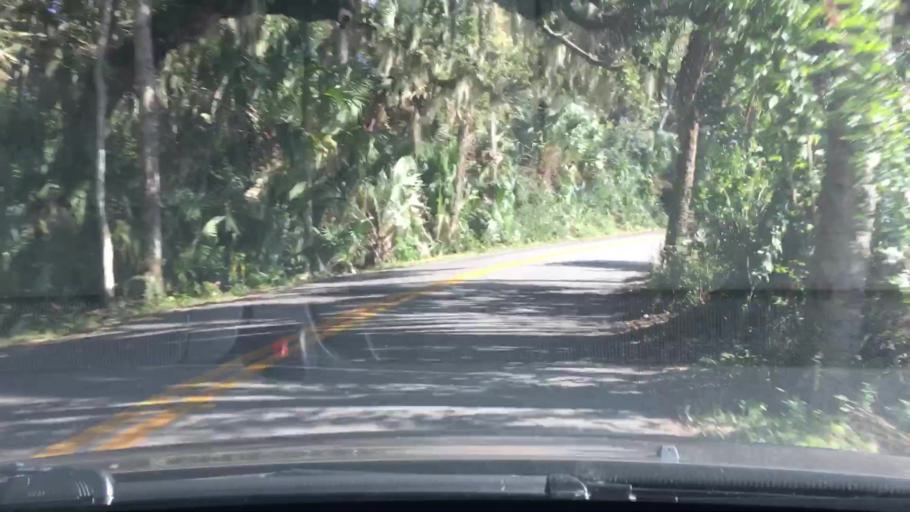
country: US
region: Florida
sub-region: Flagler County
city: Flagler Beach
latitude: 29.4053
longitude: -81.1157
